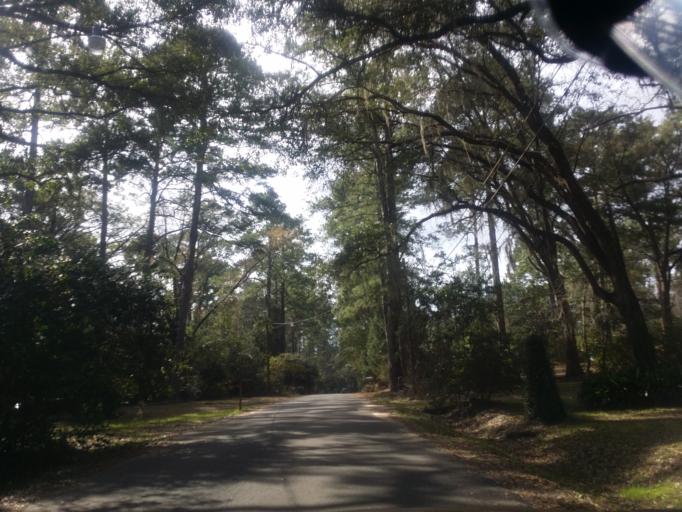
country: US
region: Florida
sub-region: Leon County
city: Tallahassee
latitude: 30.4464
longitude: -84.2402
